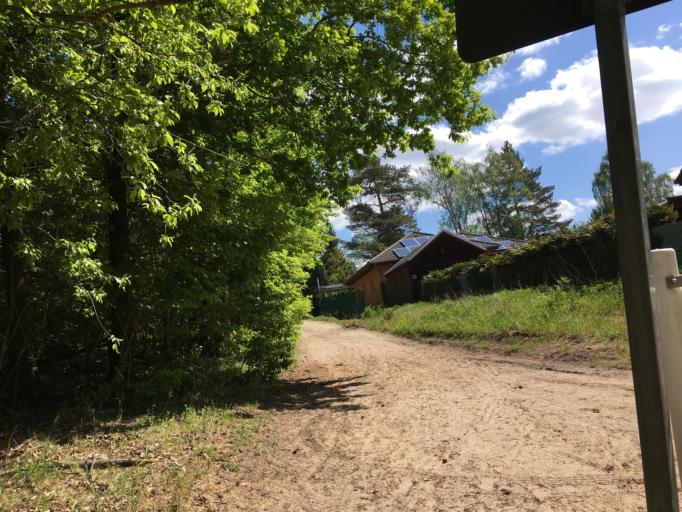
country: DE
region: Berlin
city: Blankenfelde
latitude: 52.6774
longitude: 13.3699
